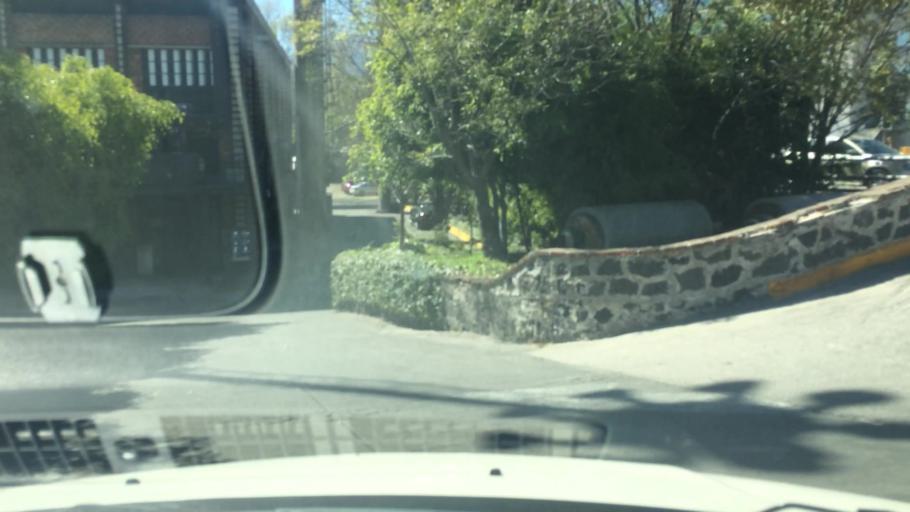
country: MX
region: Mexico City
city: Tlalpan
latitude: 19.2990
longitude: -99.1818
